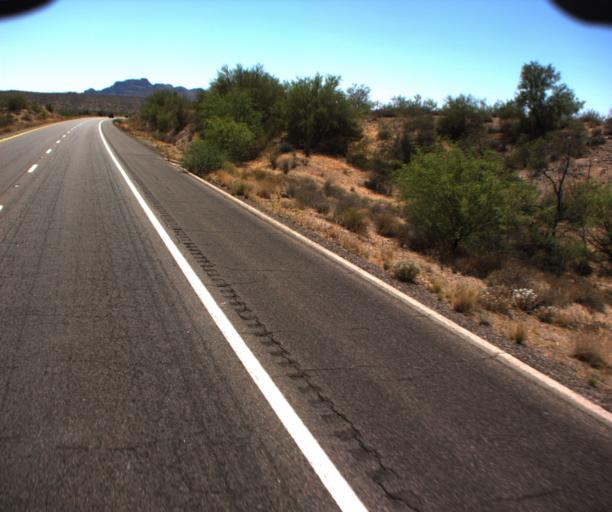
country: US
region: Arizona
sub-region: Maricopa County
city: Fountain Hills
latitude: 33.5901
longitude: -111.5994
